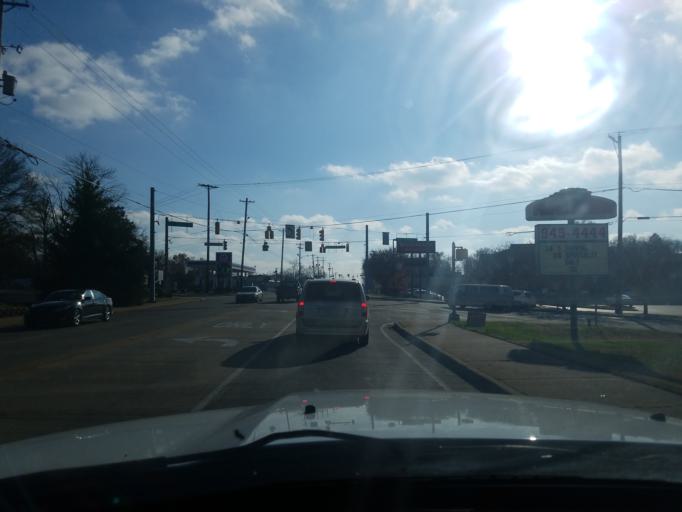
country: US
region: Indiana
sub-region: Floyd County
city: New Albany
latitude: 38.3253
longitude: -85.8009
